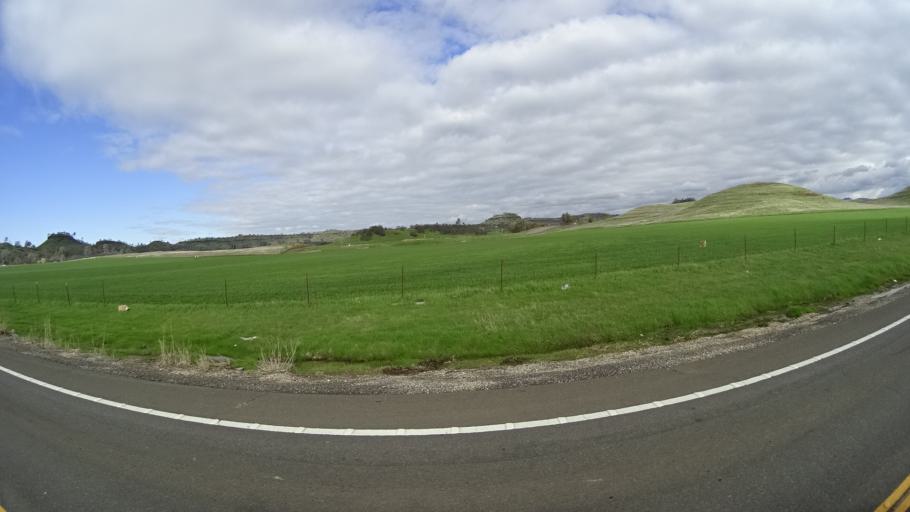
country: US
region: California
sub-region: Butte County
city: Paradise
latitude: 39.6414
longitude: -121.6542
